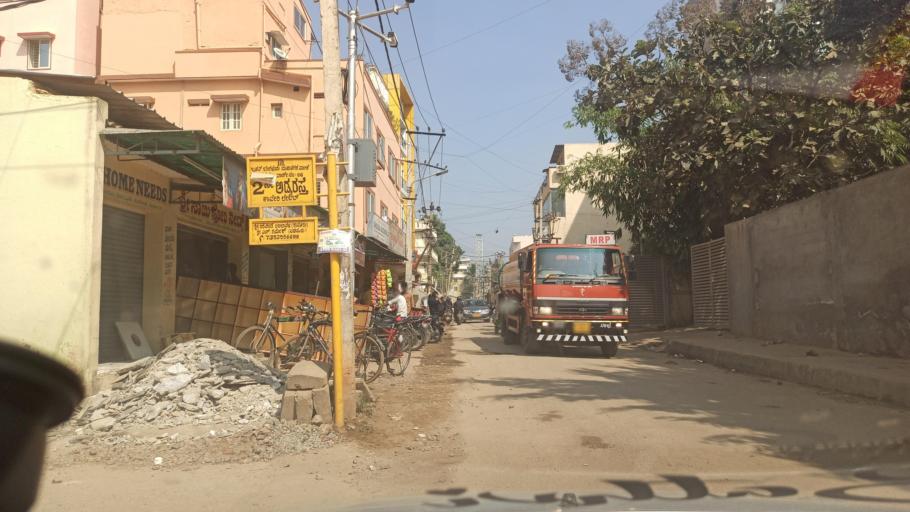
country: IN
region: Karnataka
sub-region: Bangalore Urban
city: Bangalore
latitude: 12.9510
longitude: 77.6978
